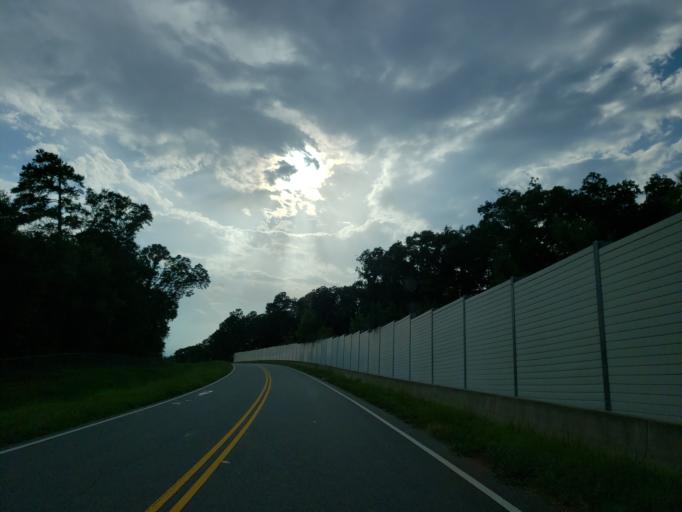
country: US
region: Georgia
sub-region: Bartow County
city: Euharlee
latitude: 34.1369
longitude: -84.9329
